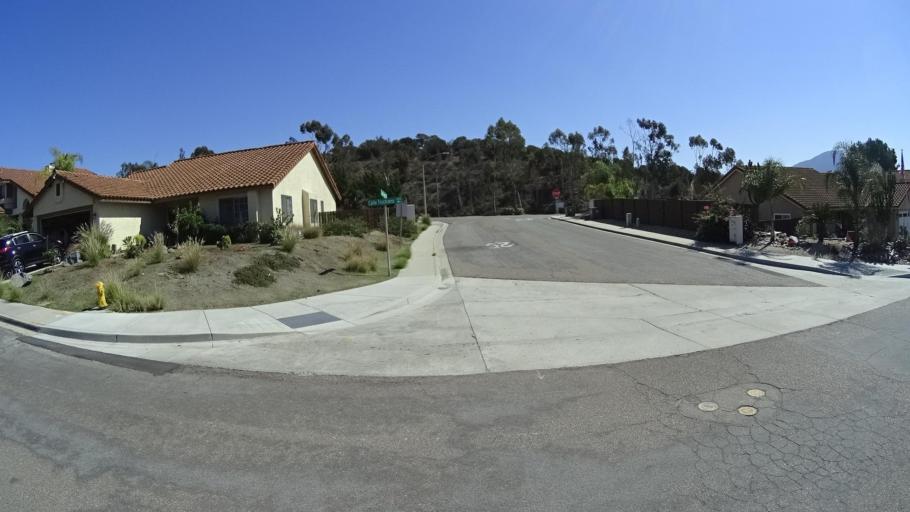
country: US
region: California
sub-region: San Diego County
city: Rancho San Diego
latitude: 32.7539
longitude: -116.9398
